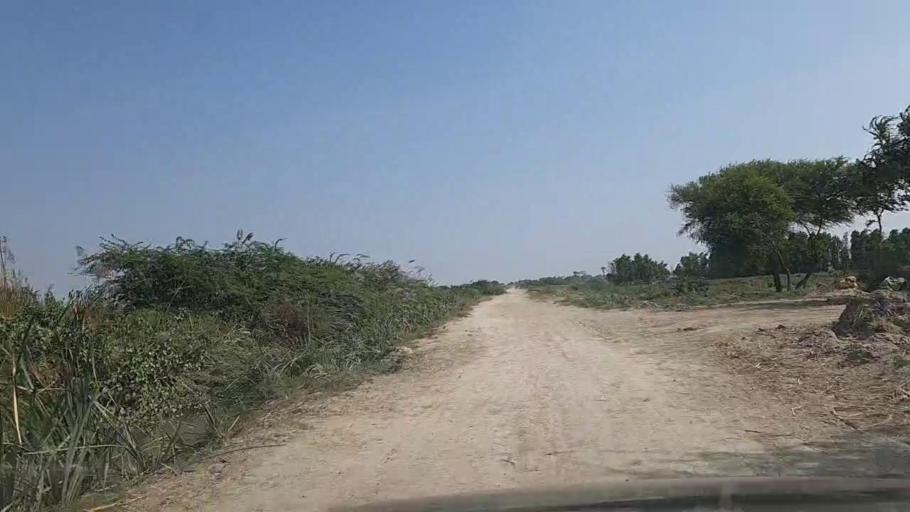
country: PK
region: Sindh
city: Gharo
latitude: 24.7134
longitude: 67.5821
